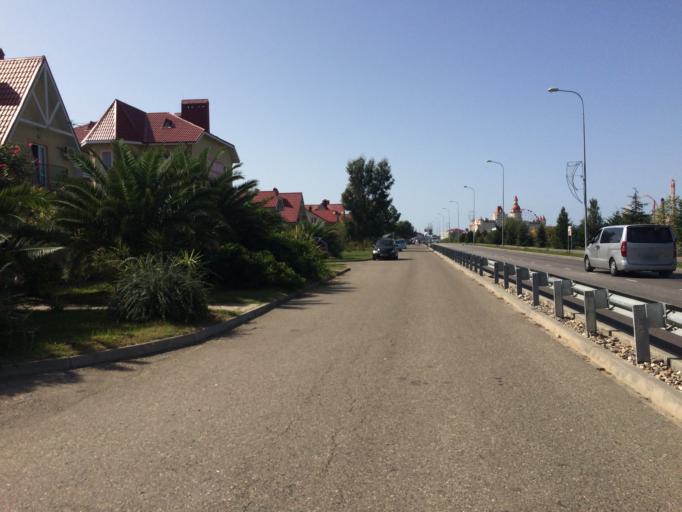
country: RU
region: Krasnodarskiy
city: Adler
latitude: 43.3989
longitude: 39.9738
